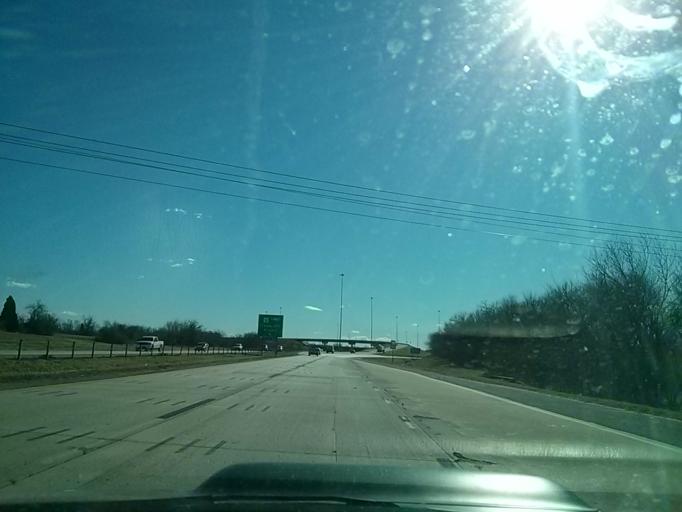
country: US
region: Oklahoma
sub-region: Tulsa County
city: Turley
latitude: 36.2060
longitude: -95.9469
